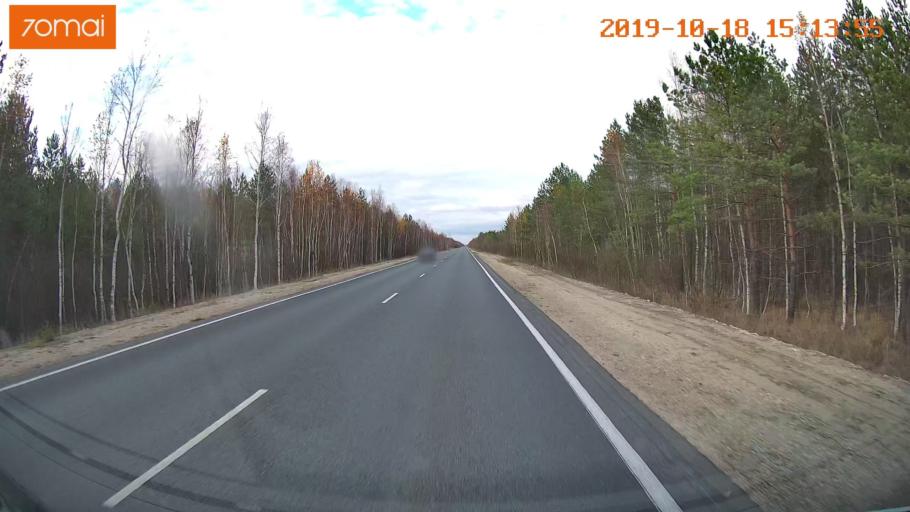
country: RU
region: Vladimir
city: Gus'-Khrustal'nyy
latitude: 55.5943
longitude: 40.7192
